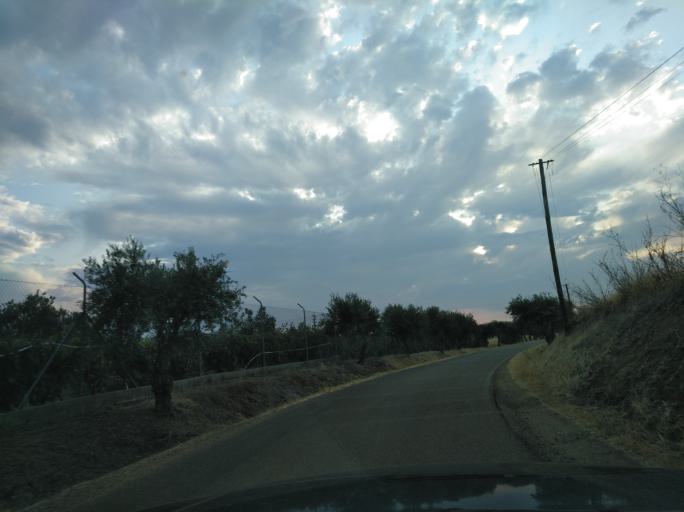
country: PT
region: Portalegre
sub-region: Campo Maior
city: Campo Maior
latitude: 39.0159
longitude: -7.0337
